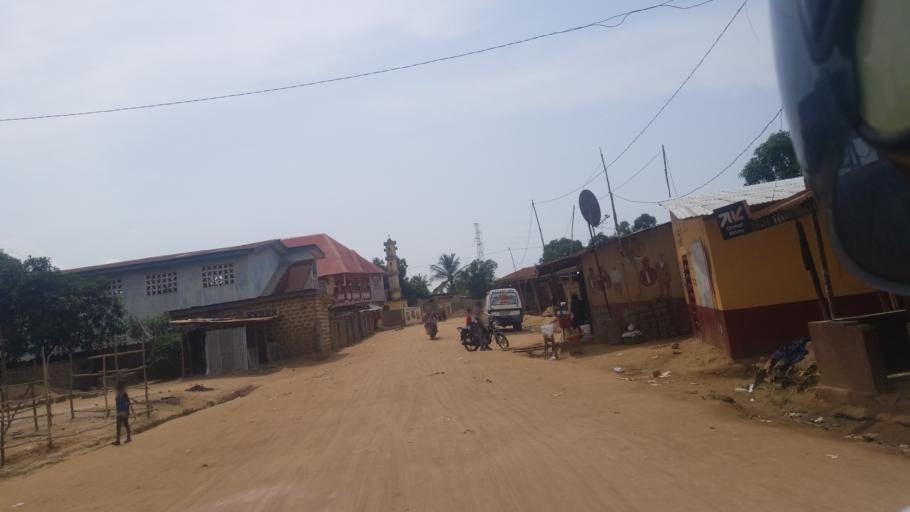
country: SL
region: Western Area
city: Waterloo
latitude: 8.3240
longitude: -13.0472
